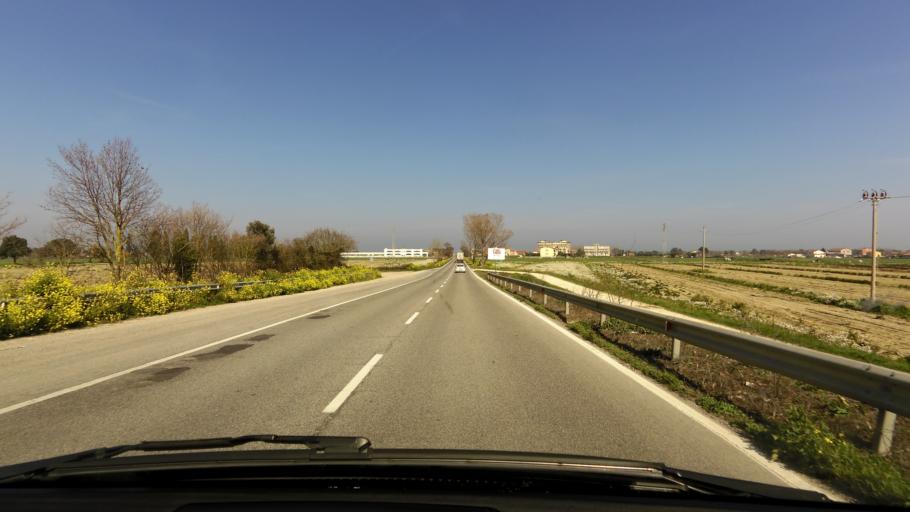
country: IT
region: The Marches
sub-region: Provincia di Macerata
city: Porto Recanati
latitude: 43.4045
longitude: 13.6674
